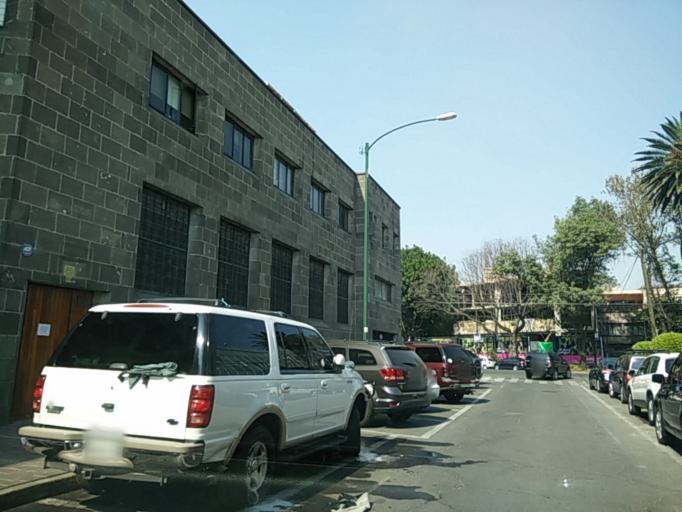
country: MX
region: Mexico City
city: Miguel Hidalgo
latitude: 19.4354
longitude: -99.1963
